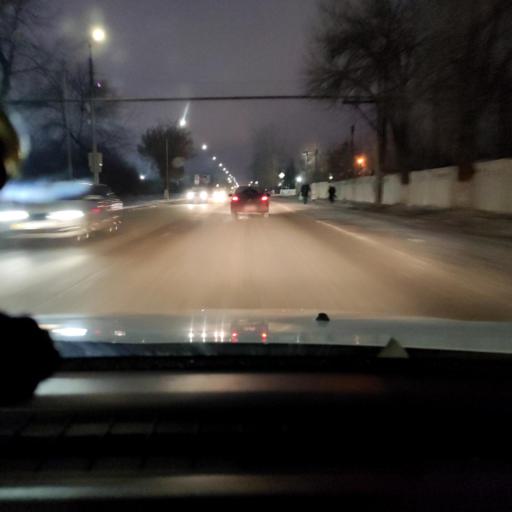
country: RU
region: Samara
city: Chapayevsk
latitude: 52.9741
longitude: 49.7021
